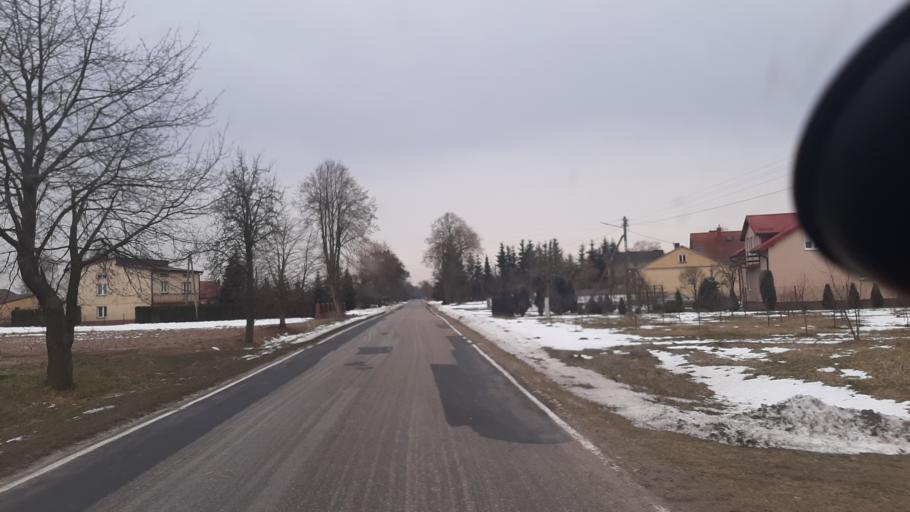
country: PL
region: Lublin Voivodeship
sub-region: Powiat lubartowski
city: Kamionka
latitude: 51.4585
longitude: 22.4207
